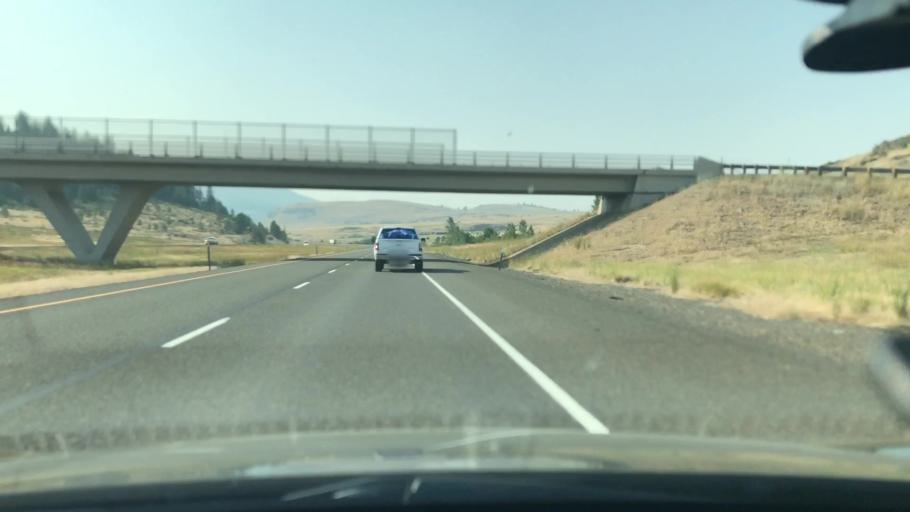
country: US
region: Oregon
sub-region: Union County
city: Union
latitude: 45.1825
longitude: -117.9863
